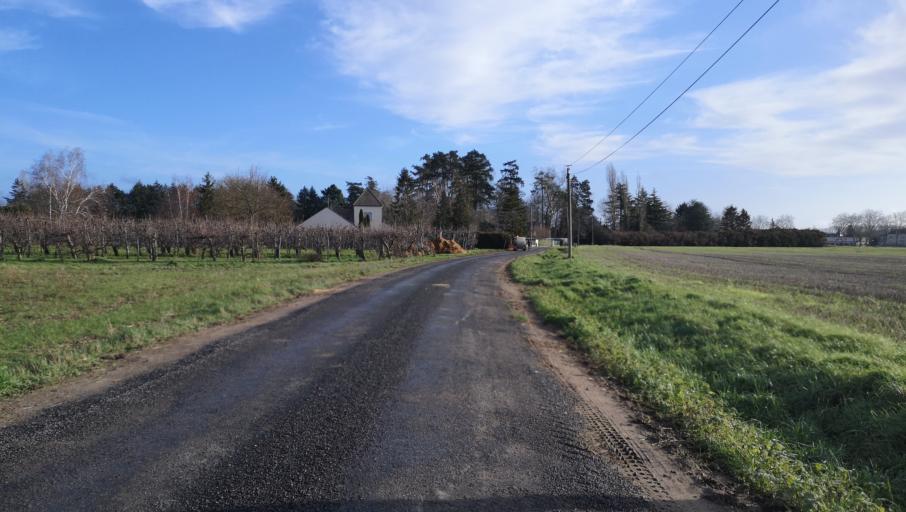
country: FR
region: Centre
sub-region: Departement du Loiret
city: La Chapelle-Saint-Mesmin
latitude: 47.8795
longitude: 1.8476
